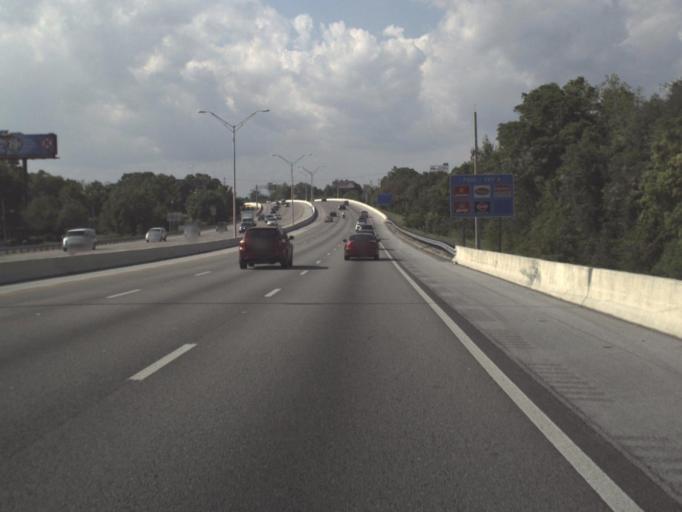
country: US
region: Florida
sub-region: Escambia County
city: Goulding
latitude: 30.4420
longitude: -87.2166
